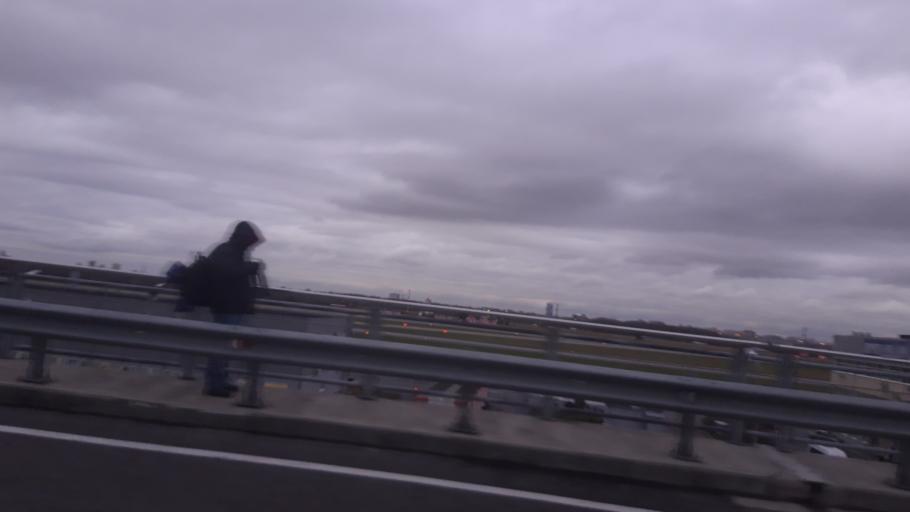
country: RU
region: St.-Petersburg
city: Dachnoye
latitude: 59.8006
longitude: 30.2747
